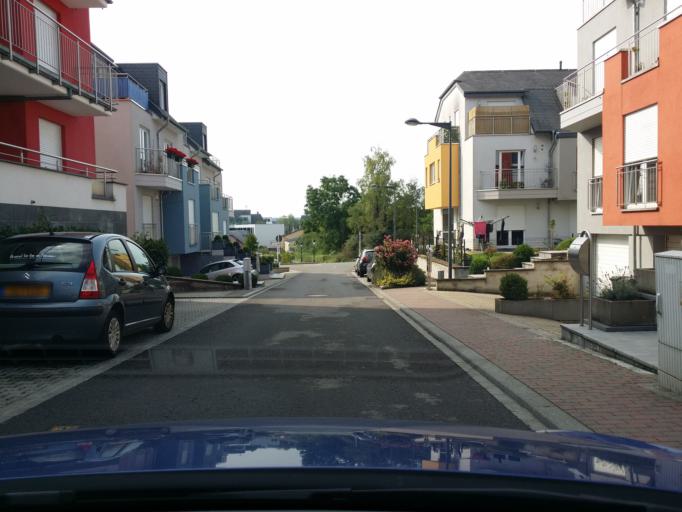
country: LU
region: Luxembourg
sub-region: Canton de Luxembourg
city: Bertrange
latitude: 49.6139
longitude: 6.0497
